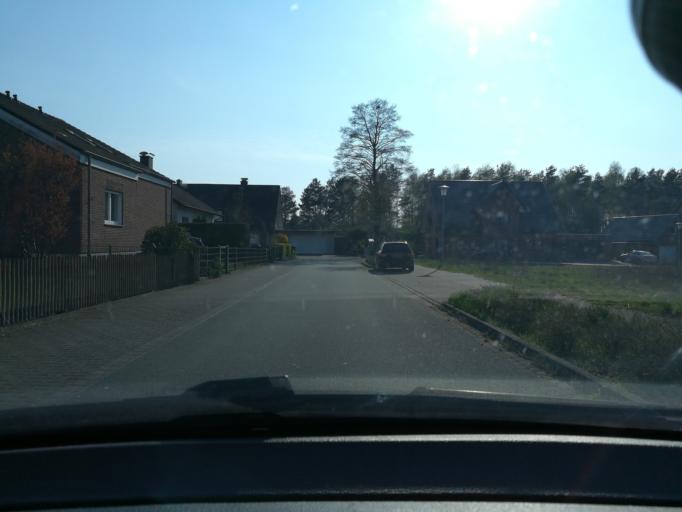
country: DE
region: North Rhine-Westphalia
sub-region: Regierungsbezirk Detmold
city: Oerlinghausen
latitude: 51.9314
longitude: 8.6000
